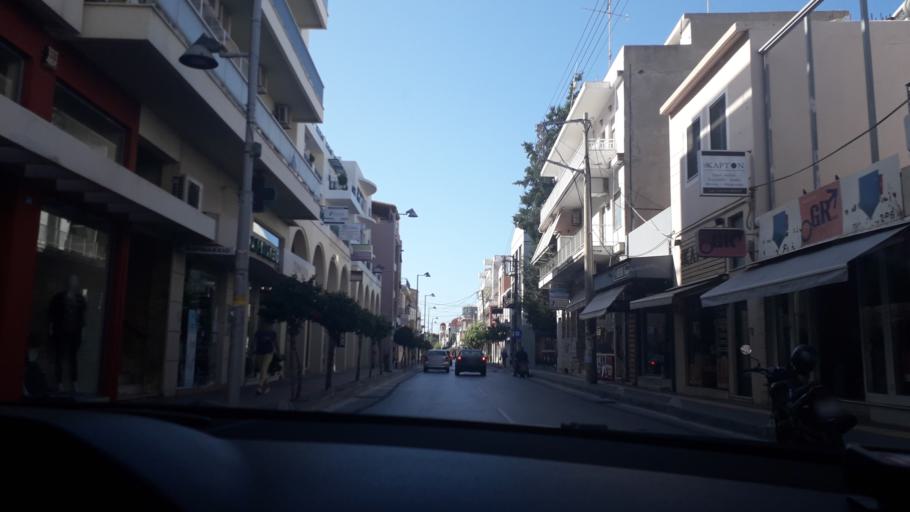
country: GR
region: Crete
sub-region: Nomos Rethymnis
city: Rethymno
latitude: 35.3656
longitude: 24.4792
